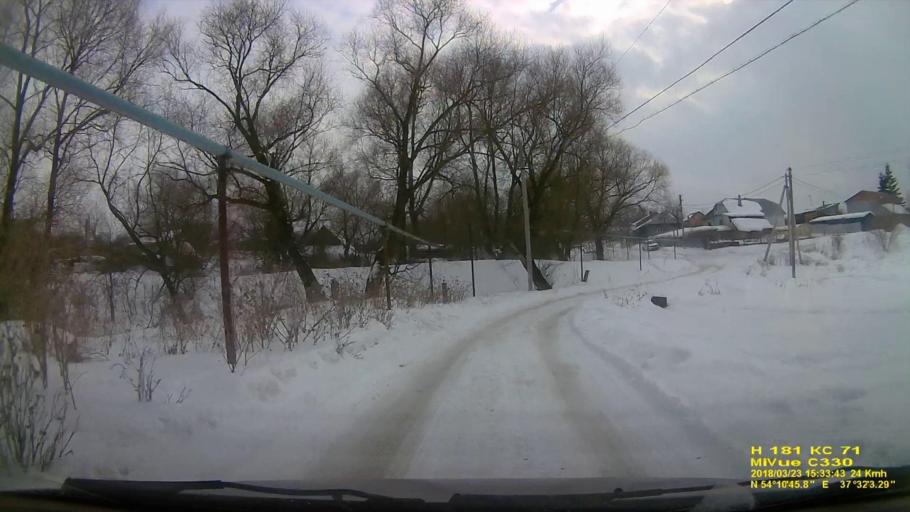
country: RU
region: Tula
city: Kosaya Gora
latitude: 54.1788
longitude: 37.5349
